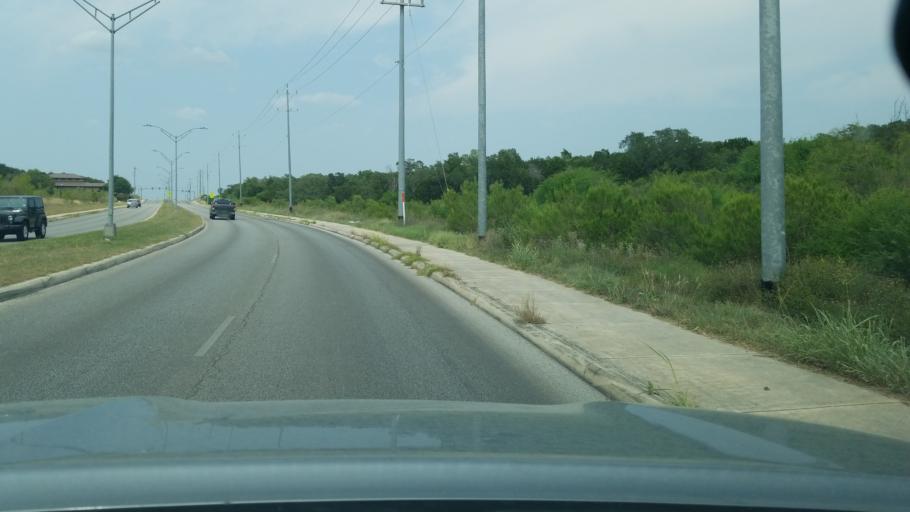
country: US
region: Texas
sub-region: Bexar County
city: Timberwood Park
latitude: 29.6546
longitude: -98.4408
